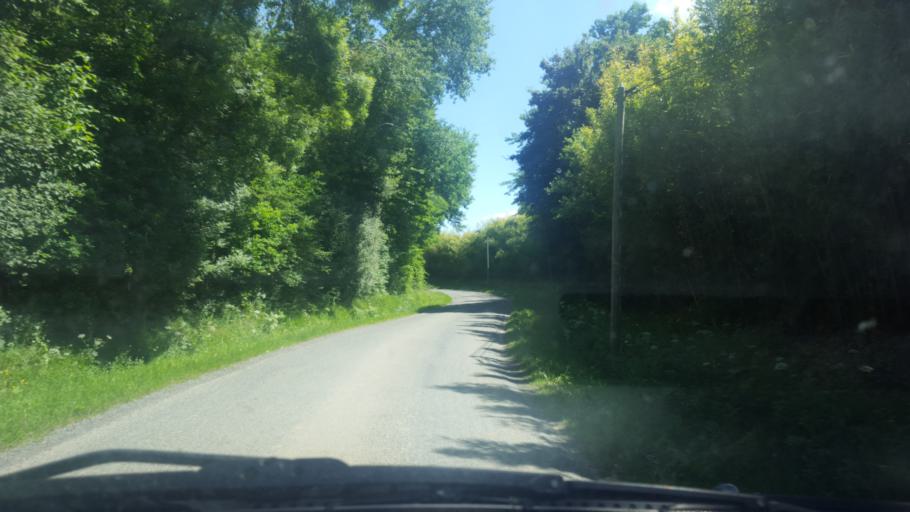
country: FR
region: Pays de la Loire
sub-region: Departement de la Loire-Atlantique
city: La Limouziniere
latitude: 47.0171
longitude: -1.6150
